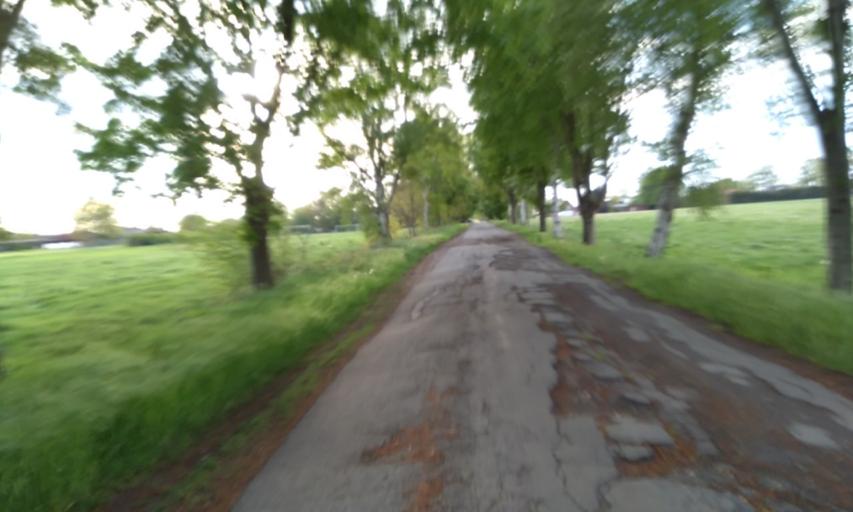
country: DE
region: Lower Saxony
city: Ahlerstedt
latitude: 53.3946
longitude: 9.4930
